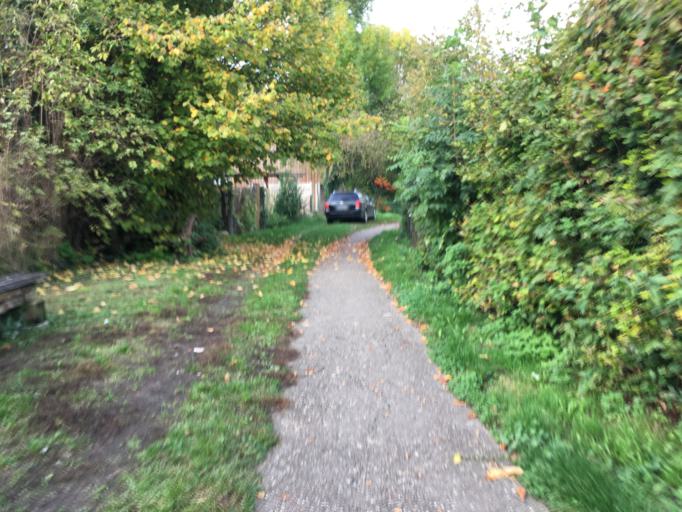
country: DE
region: Baden-Wuerttemberg
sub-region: Regierungsbezirk Stuttgart
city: Ittlingen
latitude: 49.2182
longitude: 8.9158
